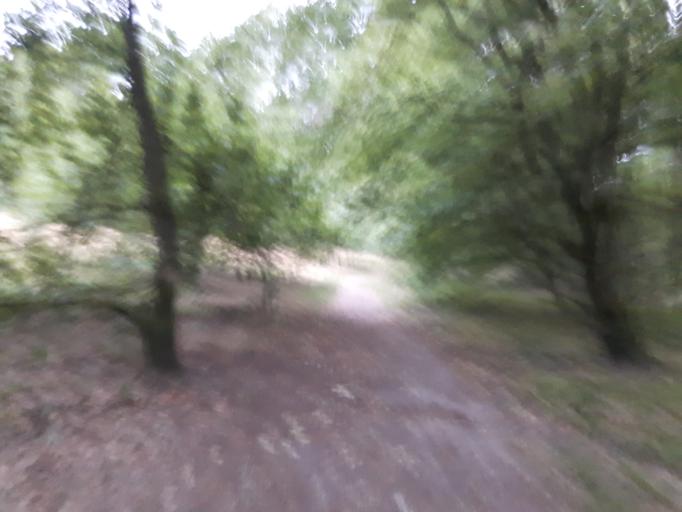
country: DE
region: Lower Saxony
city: Delmenhorst
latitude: 53.0154
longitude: 8.6850
